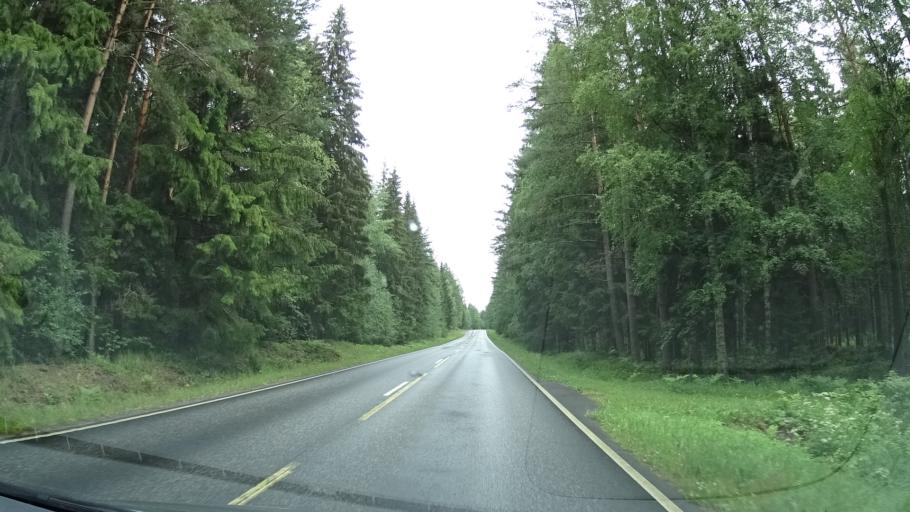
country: FI
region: Haeme
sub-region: Forssa
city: Humppila
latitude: 61.0977
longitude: 23.3369
